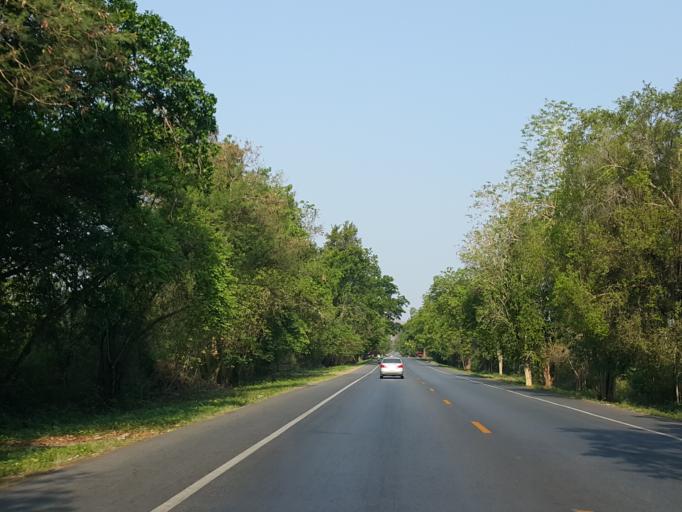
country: TH
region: Kanchanaburi
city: Sai Yok
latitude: 14.0899
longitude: 99.2964
